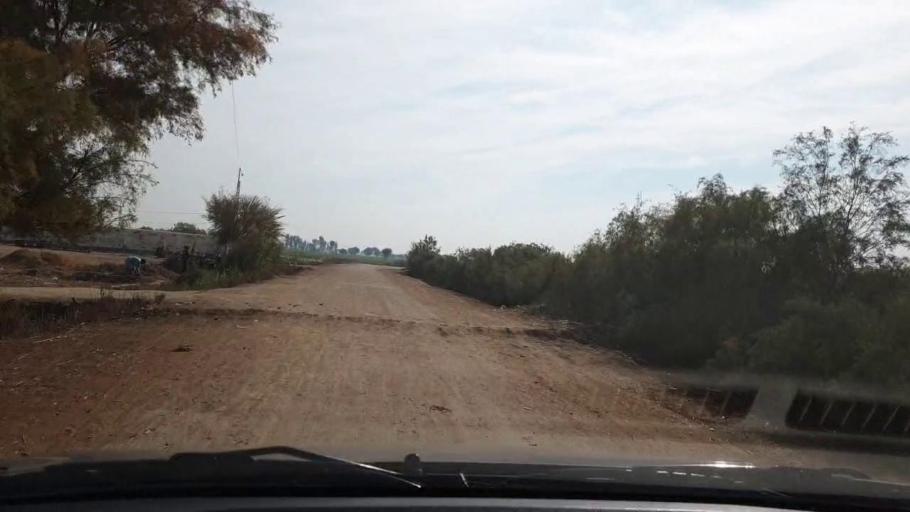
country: PK
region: Sindh
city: Shahpur Chakar
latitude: 26.1728
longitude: 68.6803
